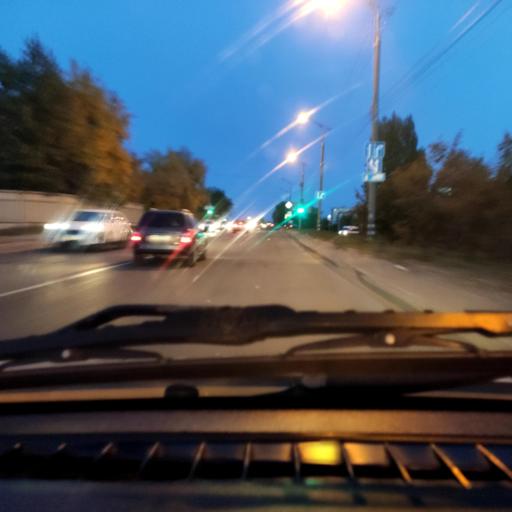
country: RU
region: Samara
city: Zhigulevsk
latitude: 53.4780
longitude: 49.5211
